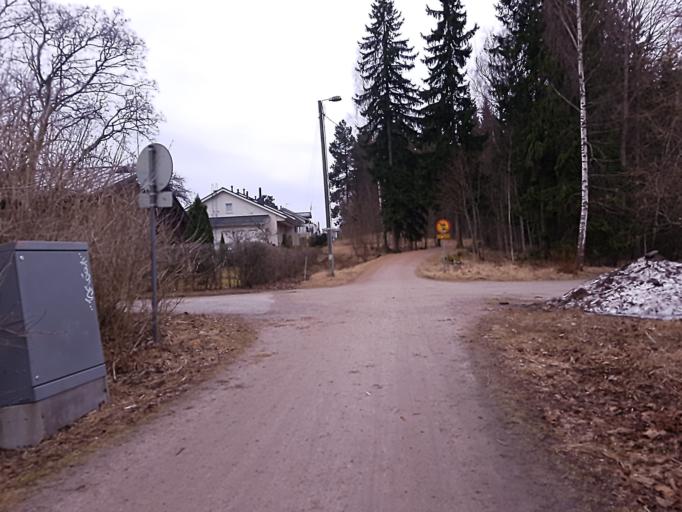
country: FI
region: Uusimaa
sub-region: Helsinki
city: Helsinki
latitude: 60.2444
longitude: 24.9124
